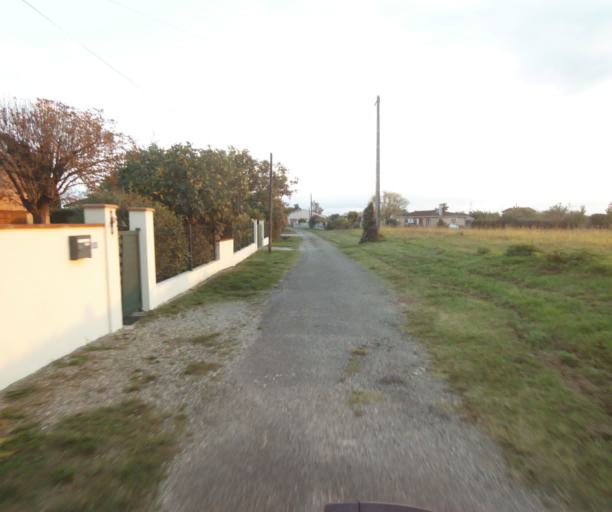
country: FR
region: Midi-Pyrenees
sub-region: Departement du Tarn-et-Garonne
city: Verdun-sur-Garonne
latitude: 43.8406
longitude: 1.2451
